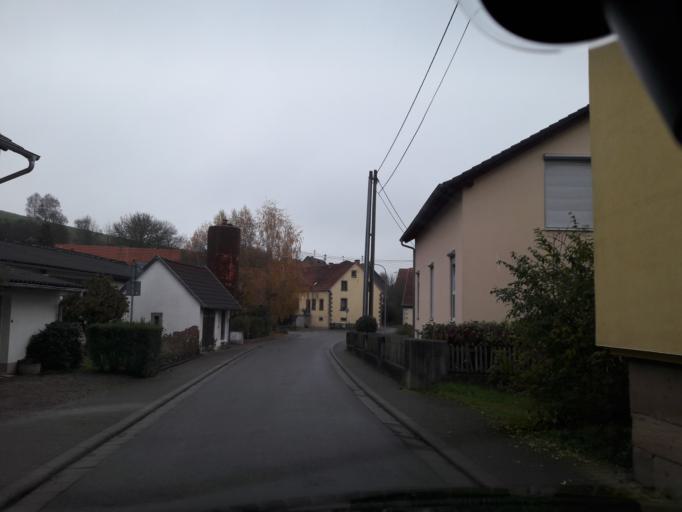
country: DE
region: Rheinland-Pfalz
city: Wahnwegen
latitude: 49.4655
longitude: 7.4046
